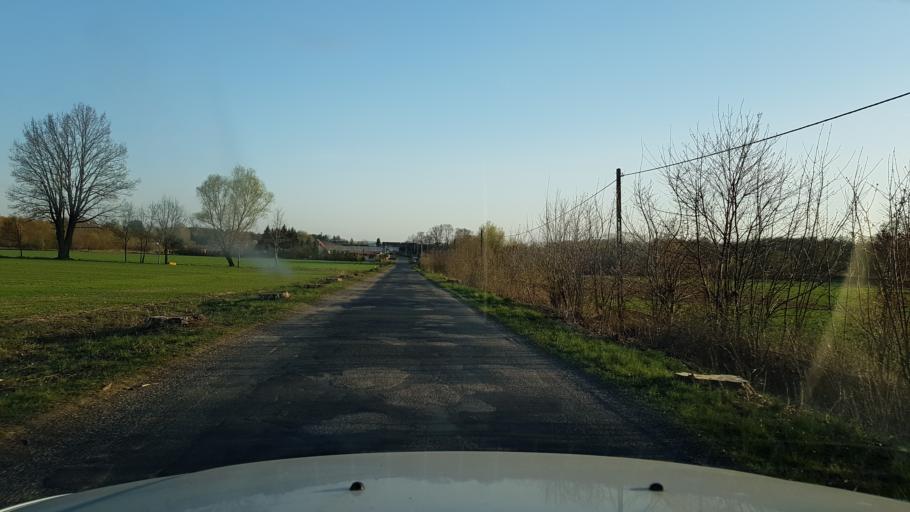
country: PL
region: West Pomeranian Voivodeship
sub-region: Powiat bialogardzki
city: Bialogard
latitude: 54.0300
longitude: 15.9891
